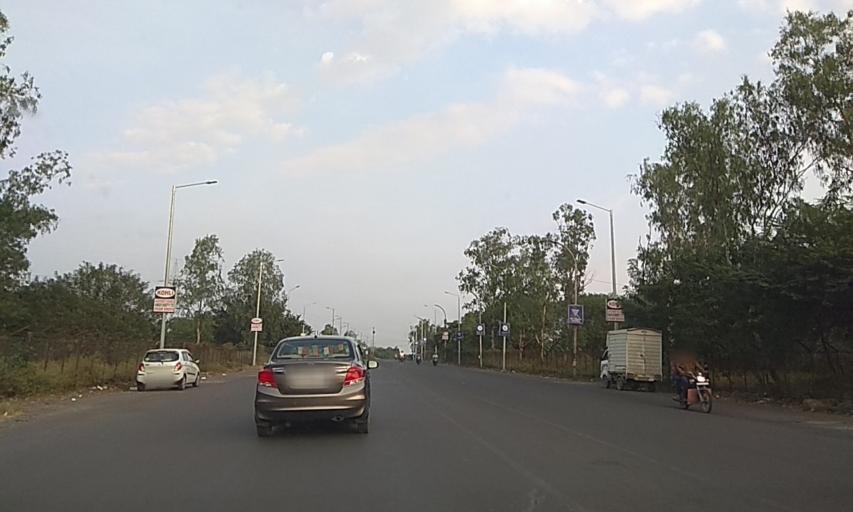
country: IN
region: Maharashtra
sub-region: Pune Division
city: Pimpri
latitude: 18.5877
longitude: 73.7872
